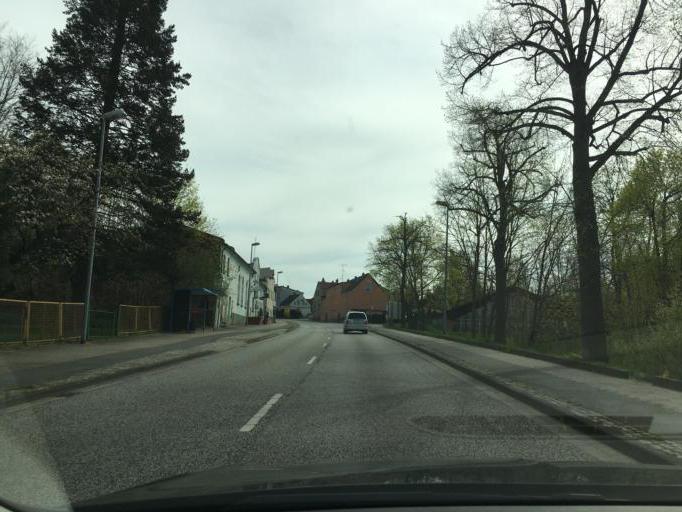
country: DE
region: Brandenburg
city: Spremberg
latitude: 51.5673
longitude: 14.3875
